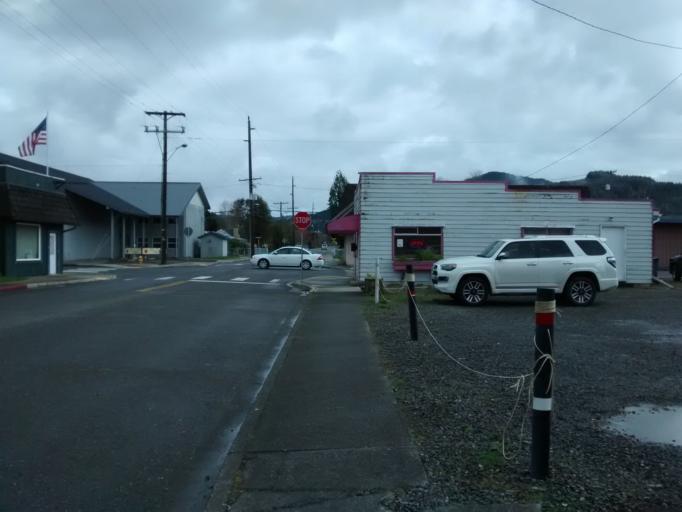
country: US
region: Washington
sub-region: Clallam County
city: Forks
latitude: 47.9504
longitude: -124.3849
